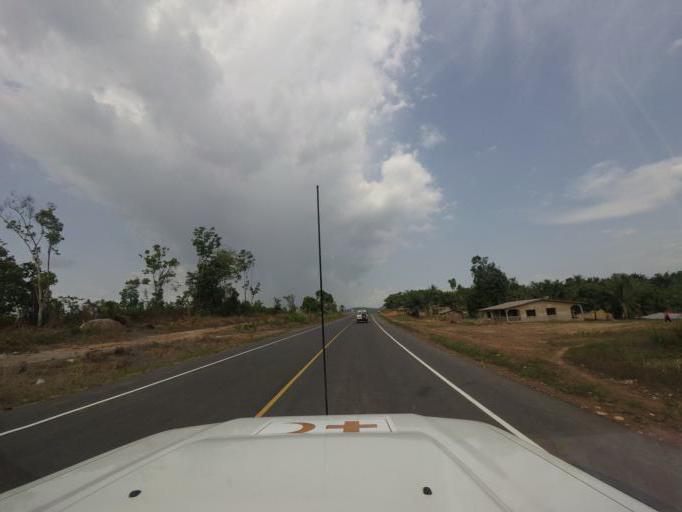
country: LR
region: Margibi
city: Kakata
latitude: 6.7657
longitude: -10.0396
